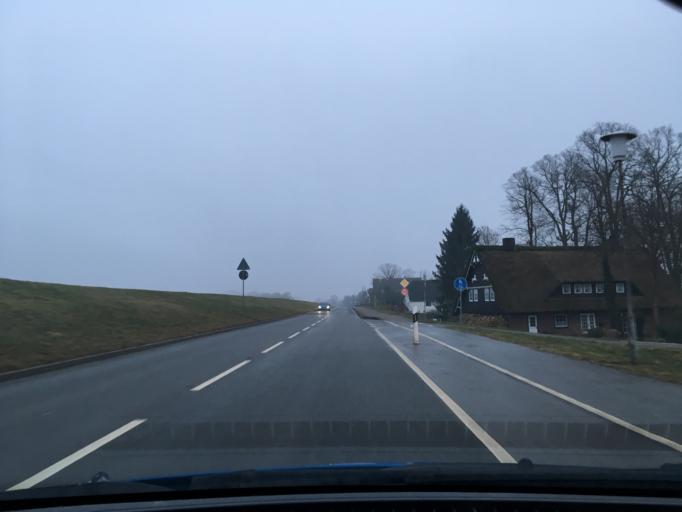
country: DE
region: Lower Saxony
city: Stelle
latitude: 53.4231
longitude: 10.1109
